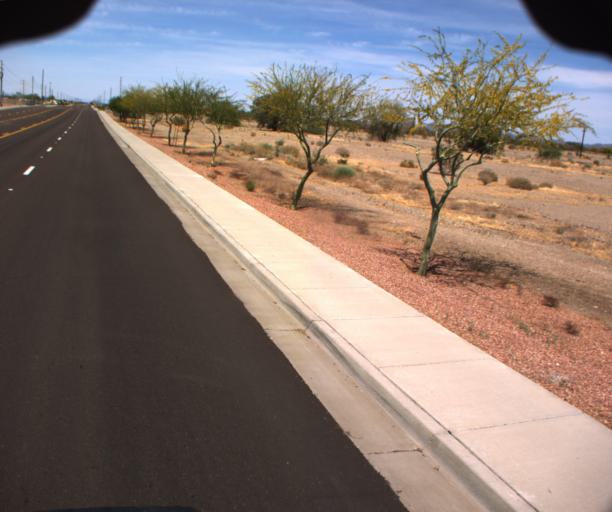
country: US
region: Arizona
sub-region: La Paz County
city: Quartzsite
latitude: 33.6793
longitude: -114.2170
